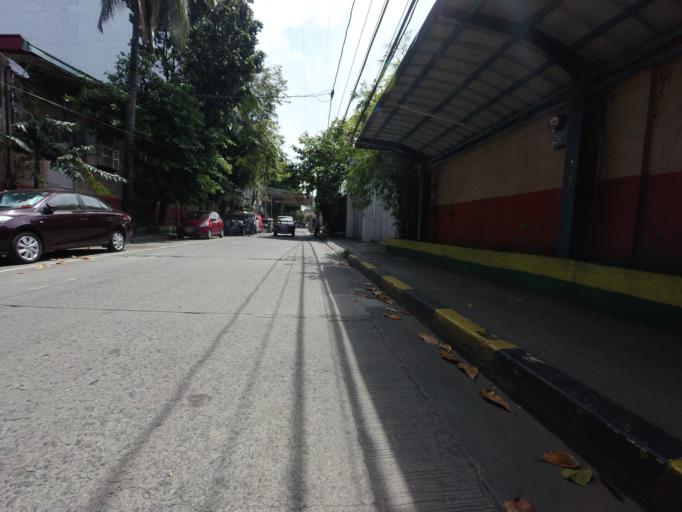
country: PH
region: Metro Manila
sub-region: Pasig
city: Pasig City
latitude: 14.5801
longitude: 121.0772
